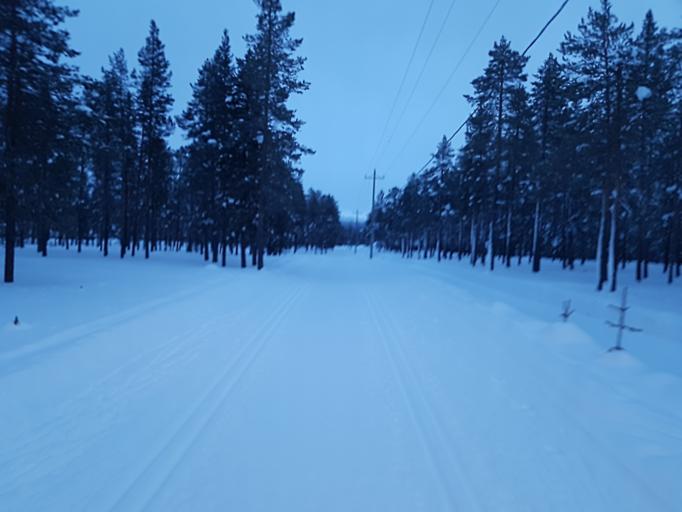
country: FI
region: Lapland
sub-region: Tunturi-Lappi
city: Kolari
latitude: 67.6206
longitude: 24.1705
